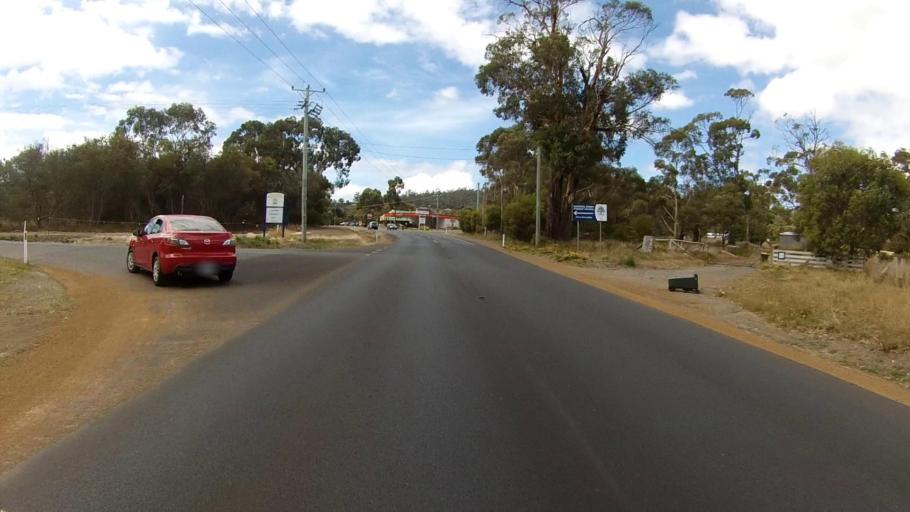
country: AU
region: Tasmania
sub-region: Sorell
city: Sorell
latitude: -42.8502
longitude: 147.6248
